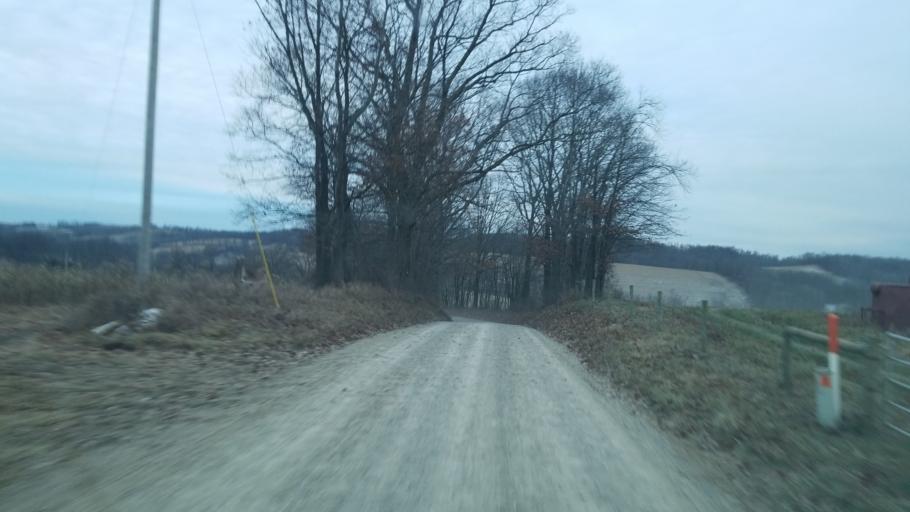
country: US
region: Ohio
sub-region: Holmes County
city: Millersburg
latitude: 40.4591
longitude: -81.8489
